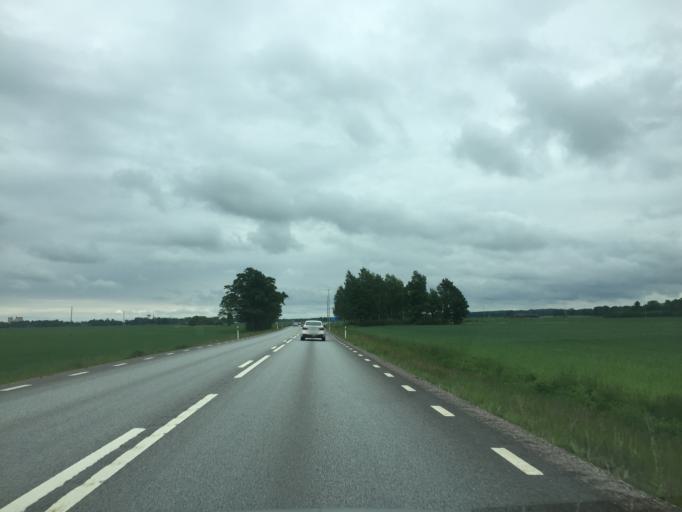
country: SE
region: OErebro
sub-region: Orebro Kommun
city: Odensbacken
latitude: 59.1538
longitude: 15.4786
